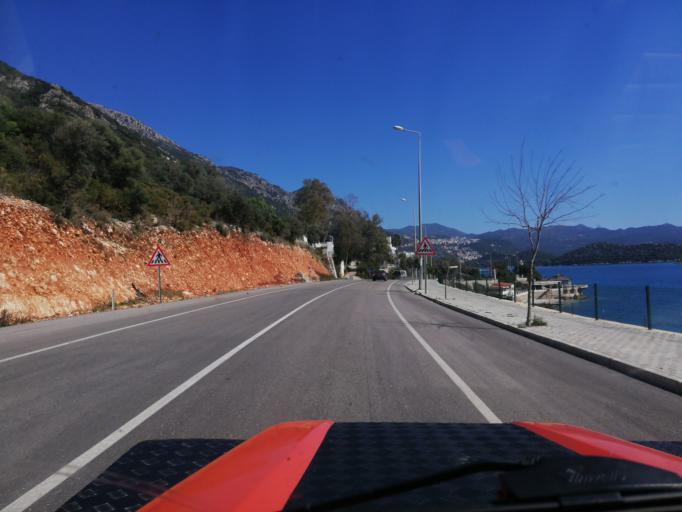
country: TR
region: Antalya
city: Kas
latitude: 36.2086
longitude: 29.6128
